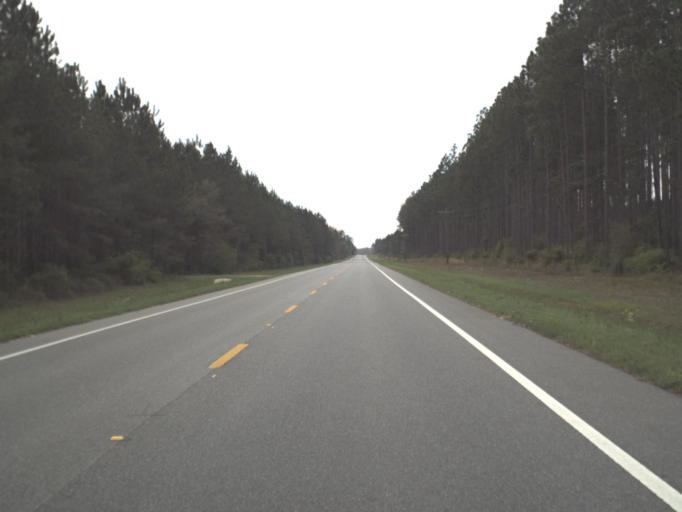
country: US
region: Florida
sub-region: Gulf County
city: Wewahitchka
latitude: 30.3090
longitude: -85.2339
